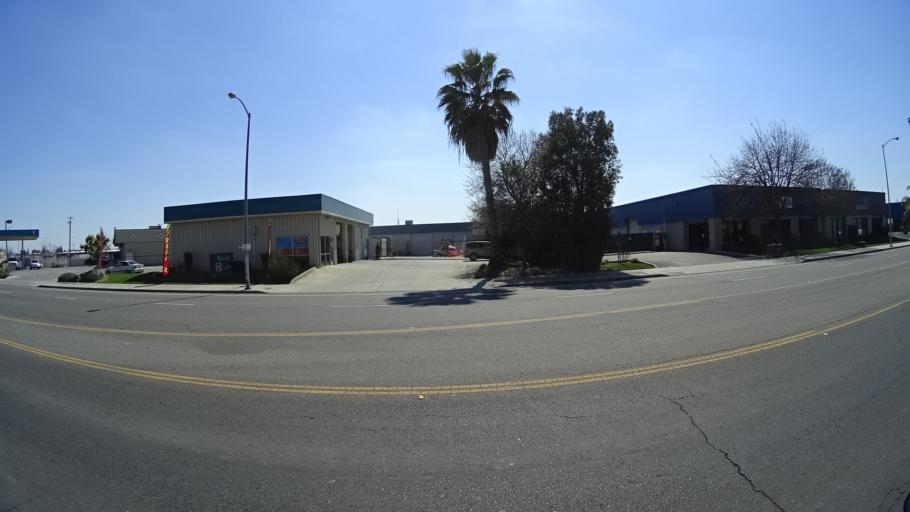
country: US
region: California
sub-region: Fresno County
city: West Park
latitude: 36.7937
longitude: -119.8543
